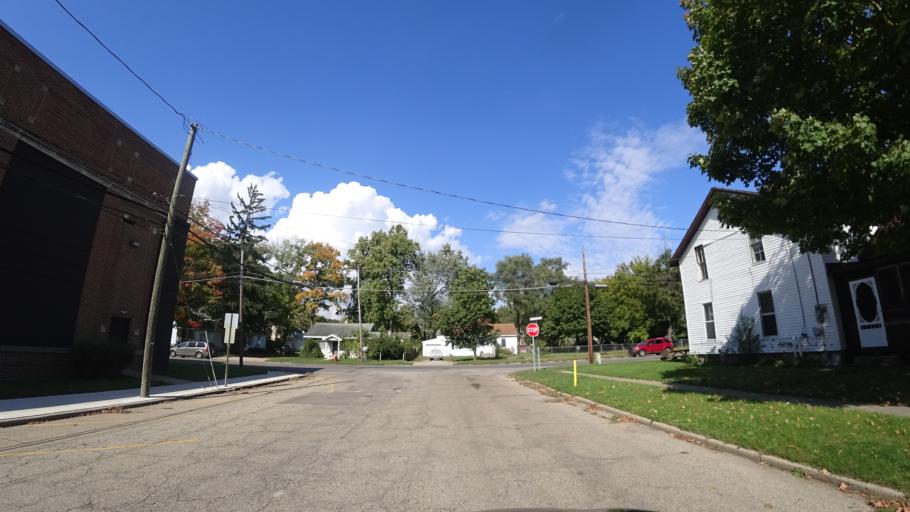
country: US
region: Michigan
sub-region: Saint Joseph County
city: Three Rivers
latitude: 41.9444
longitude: -85.6273
